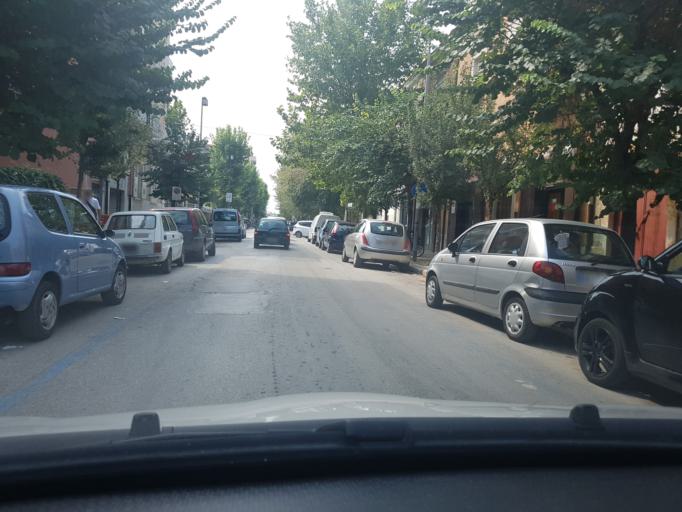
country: IT
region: Apulia
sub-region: Provincia di Foggia
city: Cerignola
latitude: 41.2664
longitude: 15.9035
